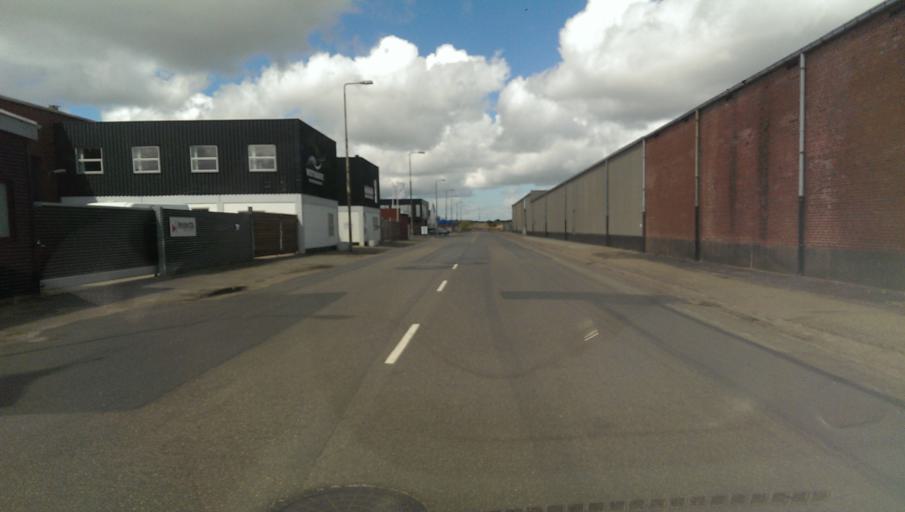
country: DK
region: South Denmark
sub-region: Esbjerg Kommune
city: Esbjerg
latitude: 55.4797
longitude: 8.4211
